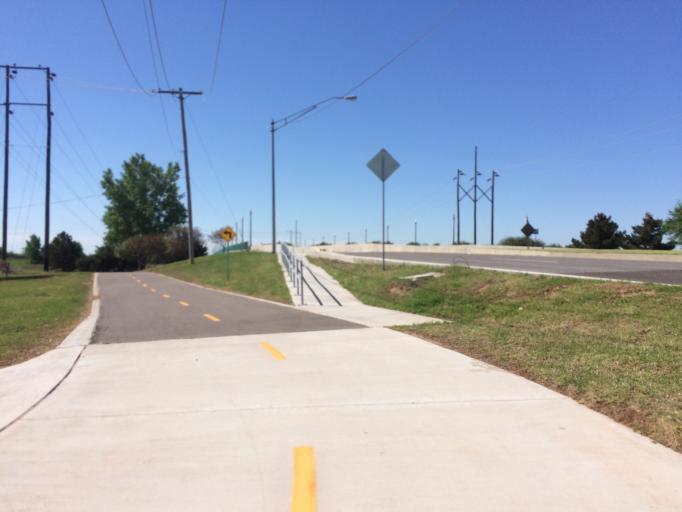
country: US
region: Oklahoma
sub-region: Oklahoma County
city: Oklahoma City
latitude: 35.4597
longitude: -97.5654
